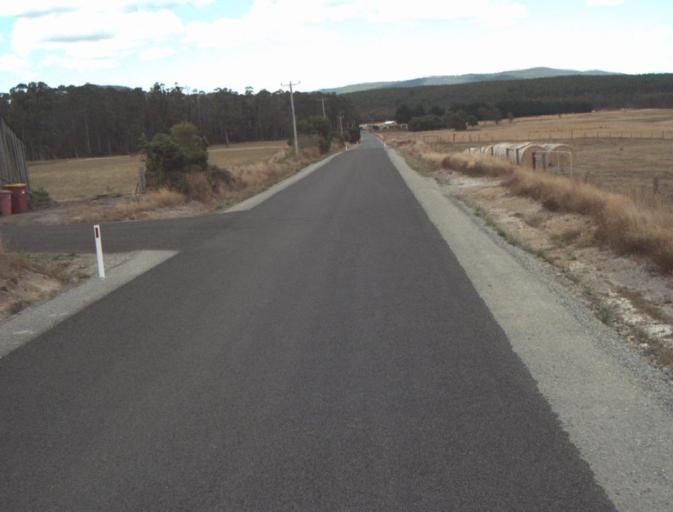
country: AU
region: Tasmania
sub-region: Launceston
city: Mayfield
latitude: -41.2009
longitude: 147.1896
